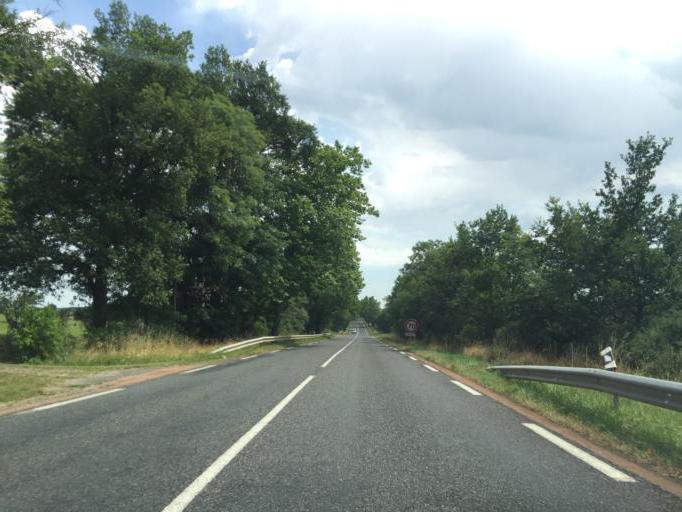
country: FR
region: Rhone-Alpes
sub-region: Departement du Rhone
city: Saint-Romain-de-Popey
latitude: 45.8710
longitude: 4.5403
